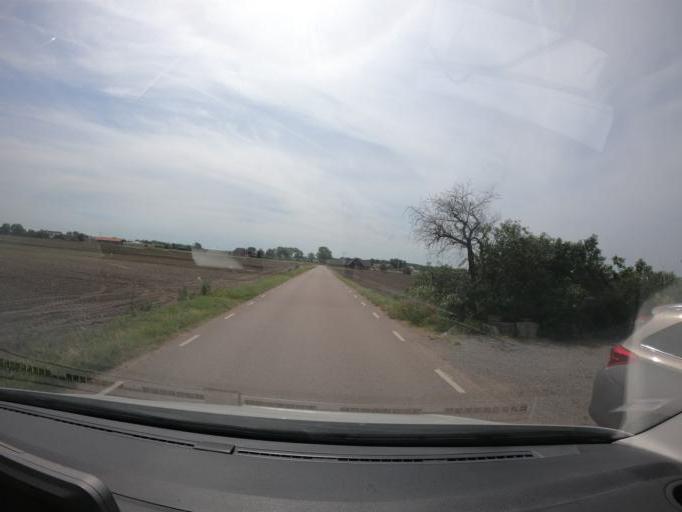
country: SE
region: Skane
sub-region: Angelholms Kommun
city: Vejbystrand
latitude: 56.3400
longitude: 12.7795
